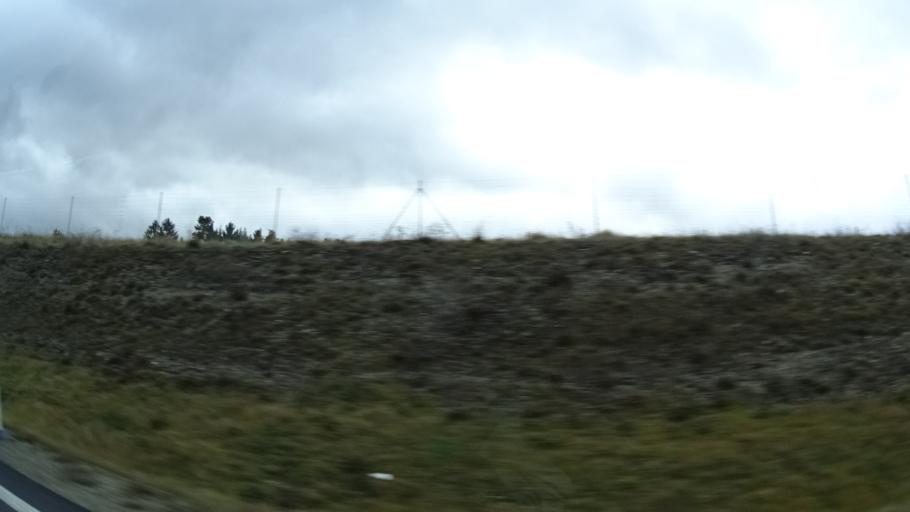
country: DE
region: Thuringia
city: Rohr
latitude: 50.5798
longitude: 10.4753
